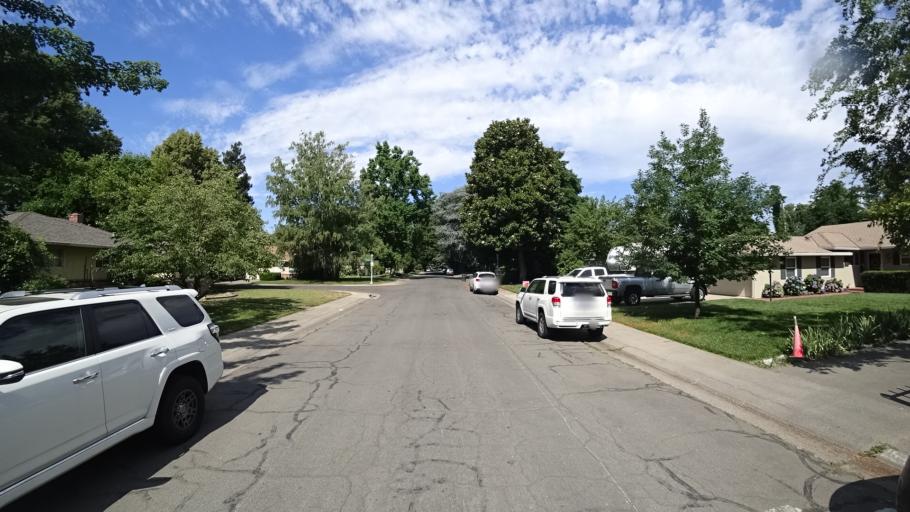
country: US
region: California
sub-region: Sacramento County
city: Arden-Arcade
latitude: 38.5803
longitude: -121.4307
